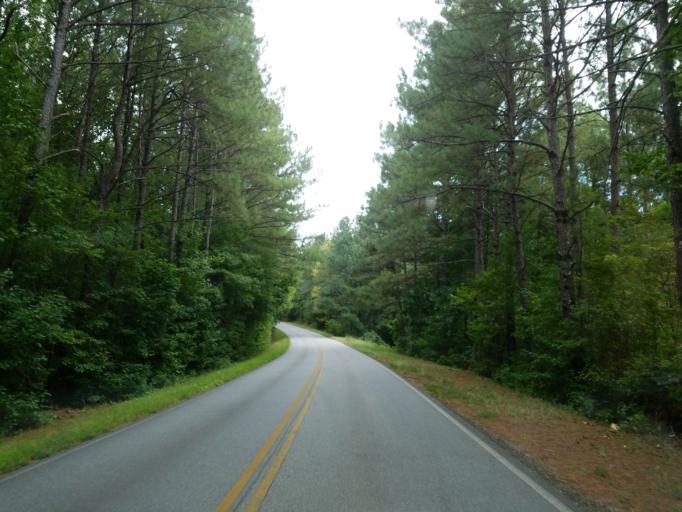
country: US
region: Georgia
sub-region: Monroe County
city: Forsyth
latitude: 32.9129
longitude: -83.9112
